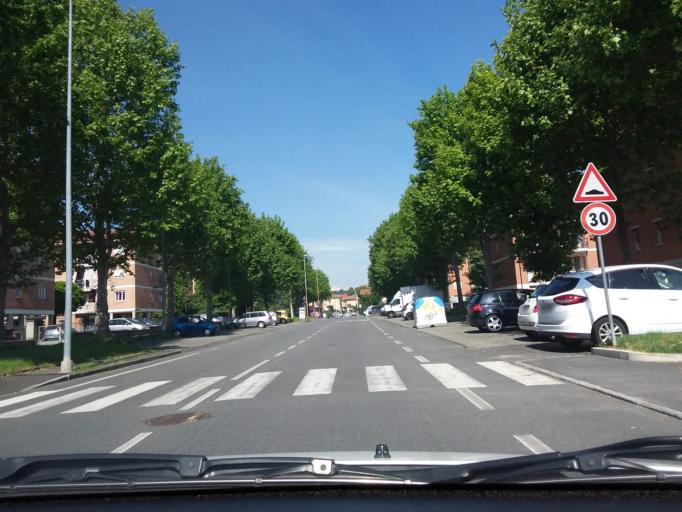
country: IT
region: Piedmont
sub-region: Provincia di Torino
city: Rivoli
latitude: 45.0754
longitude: 7.5082
